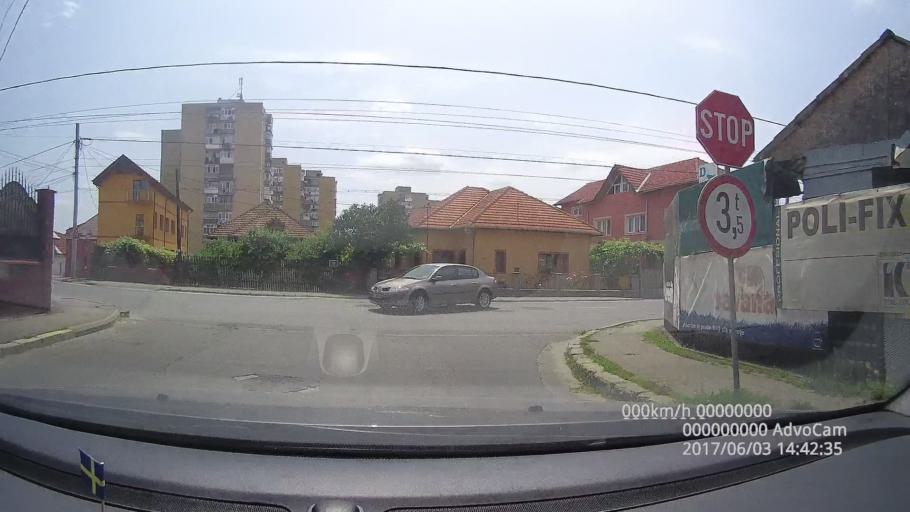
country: RO
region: Gorj
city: Targu Jiu
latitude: 45.0255
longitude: 23.2685
